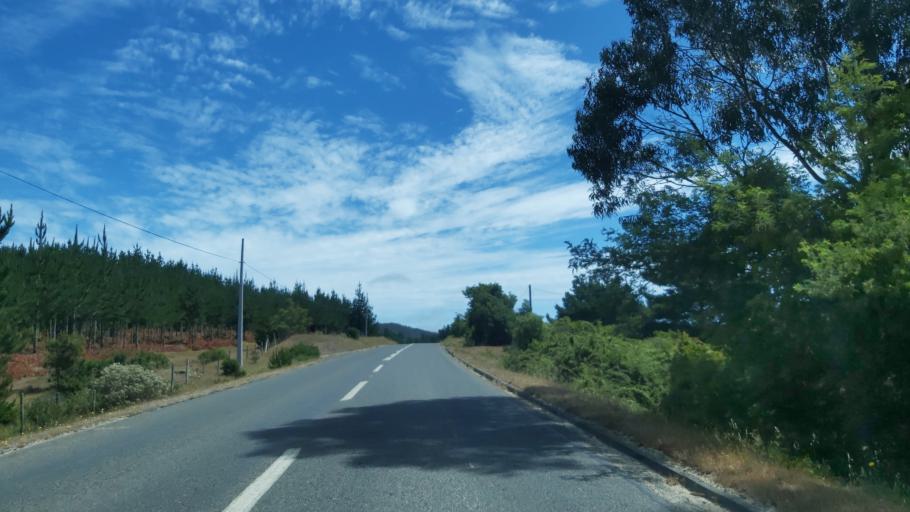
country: CL
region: Maule
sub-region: Provincia de Talca
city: Constitucion
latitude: -35.5565
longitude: -72.5836
